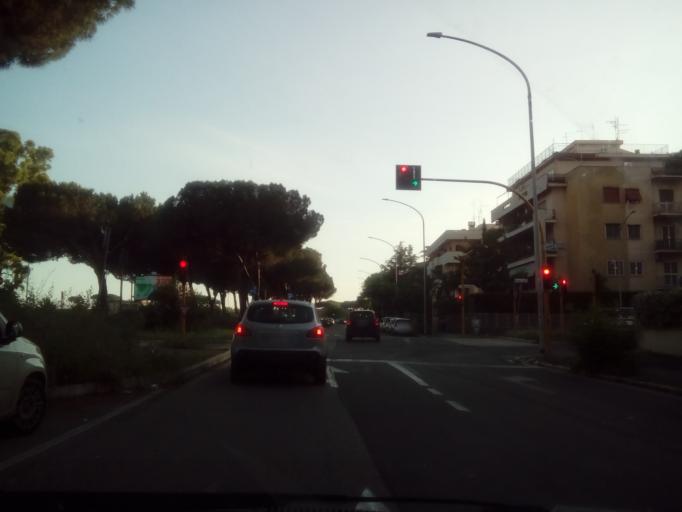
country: IT
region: Latium
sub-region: Citta metropolitana di Roma Capitale
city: Ciampino
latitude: 41.8507
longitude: 12.5674
